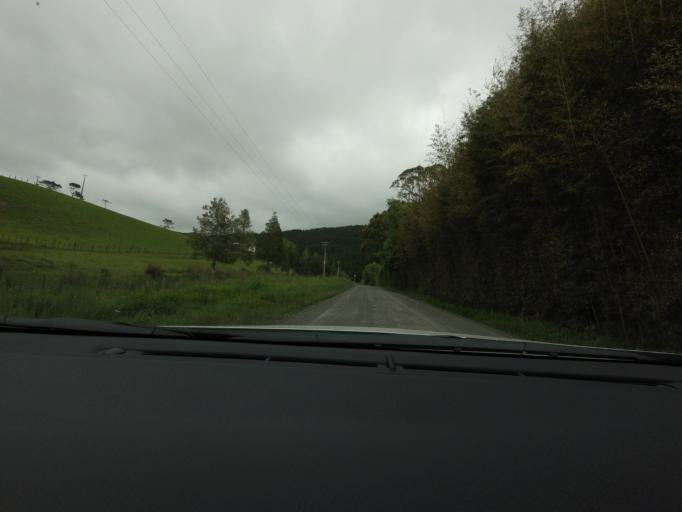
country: NZ
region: Auckland
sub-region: Auckland
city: Warkworth
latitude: -36.4712
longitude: 174.5532
